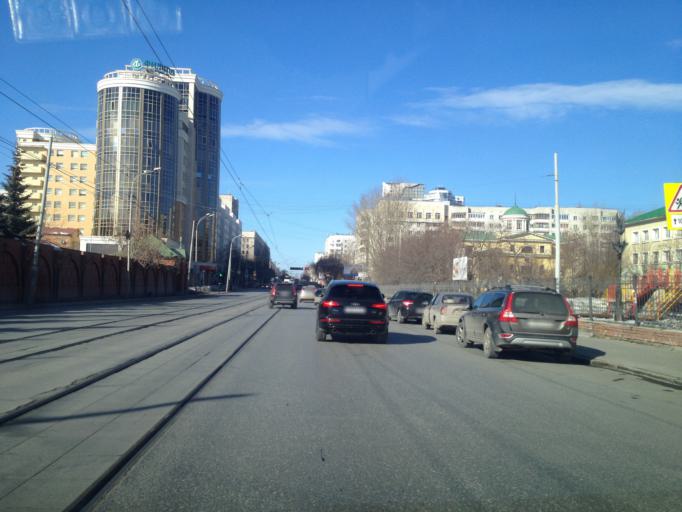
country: RU
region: Sverdlovsk
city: Yekaterinburg
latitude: 56.8325
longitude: 60.6233
